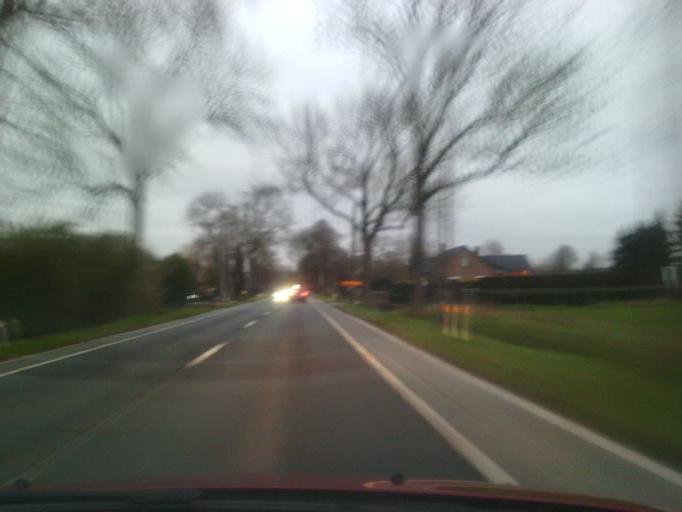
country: BE
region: Flanders
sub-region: Provincie Oost-Vlaanderen
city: Waasmunster
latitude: 51.0958
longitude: 4.0908
